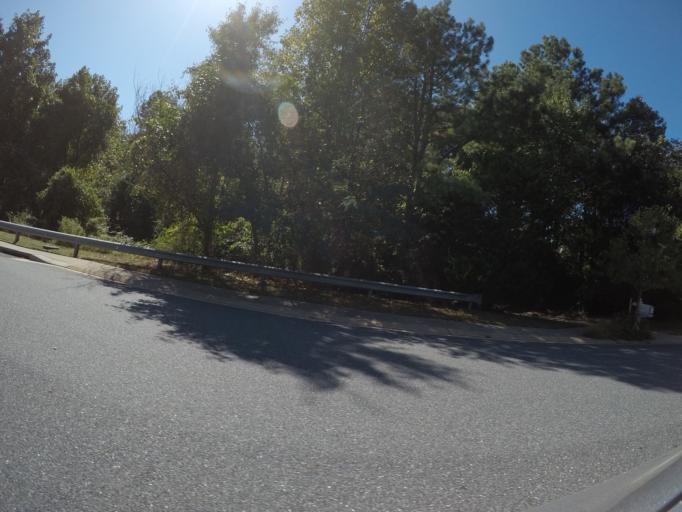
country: US
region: Maryland
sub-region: Harford County
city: Riverside
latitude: 39.4778
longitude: -76.2815
